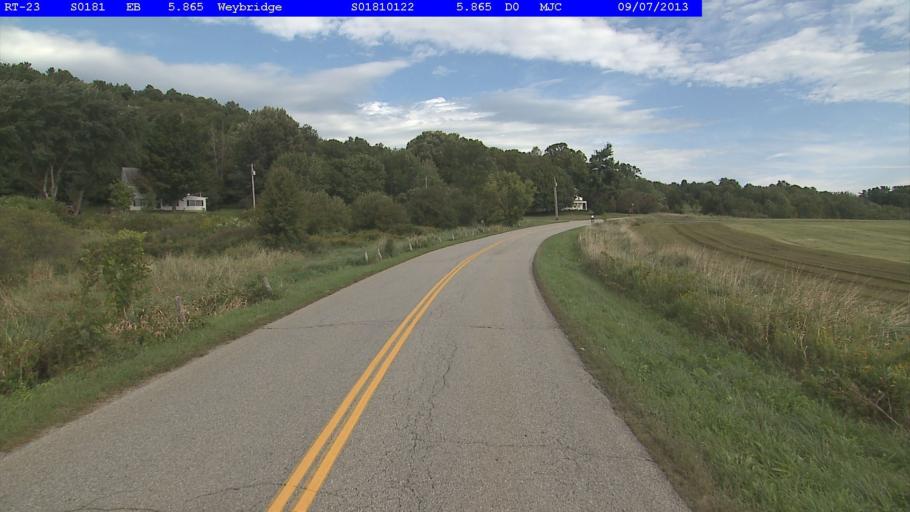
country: US
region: Vermont
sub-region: Addison County
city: Vergennes
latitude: 44.0748
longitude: -73.2540
